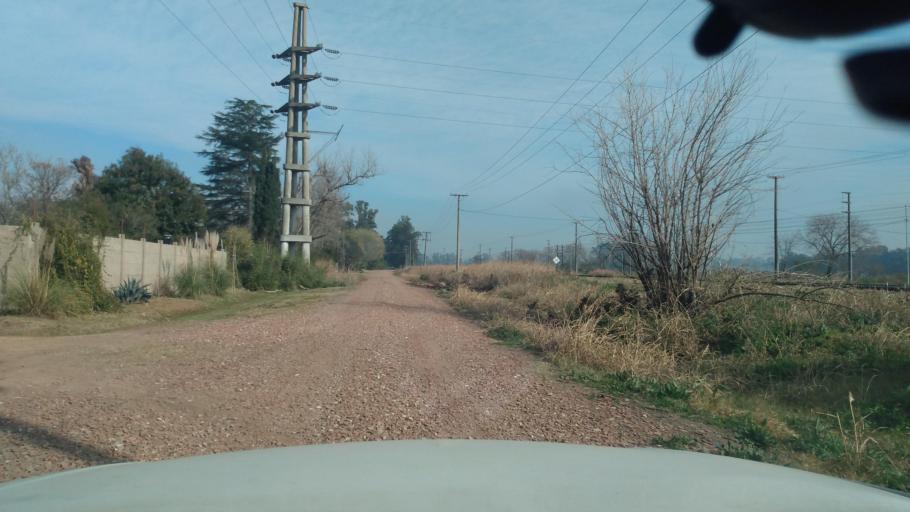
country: AR
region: Buenos Aires
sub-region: Partido de Lujan
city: Lujan
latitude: -34.5892
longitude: -59.1385
